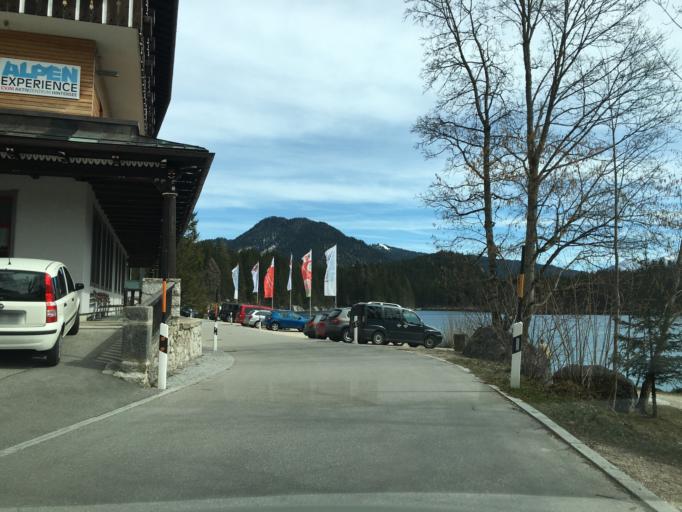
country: DE
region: Bavaria
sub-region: Upper Bavaria
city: Ramsau
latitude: 47.6069
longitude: 12.8511
